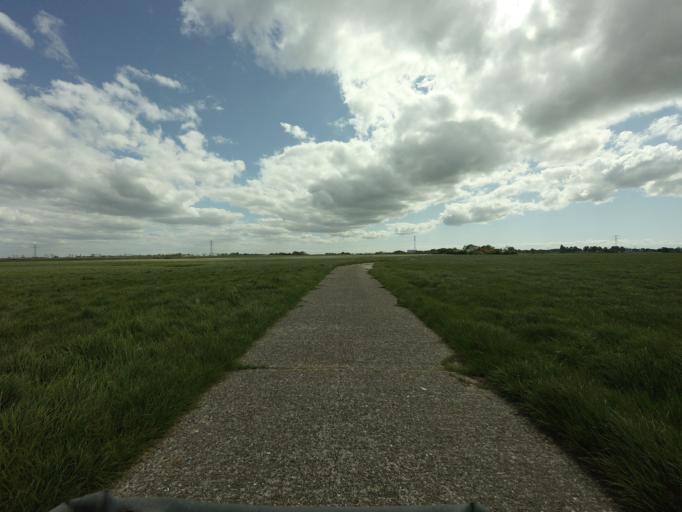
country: NL
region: Friesland
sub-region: Sudwest Fryslan
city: Bolsward
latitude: 53.0773
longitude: 5.5491
